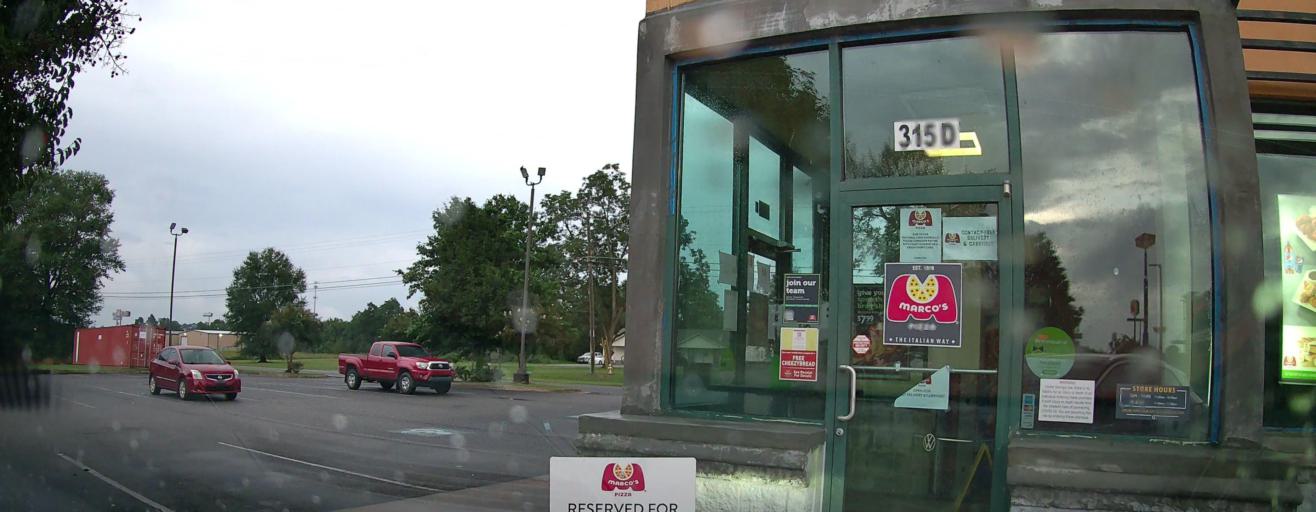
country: US
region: Georgia
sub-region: Peach County
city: Byron
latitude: 32.6632
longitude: -83.7407
